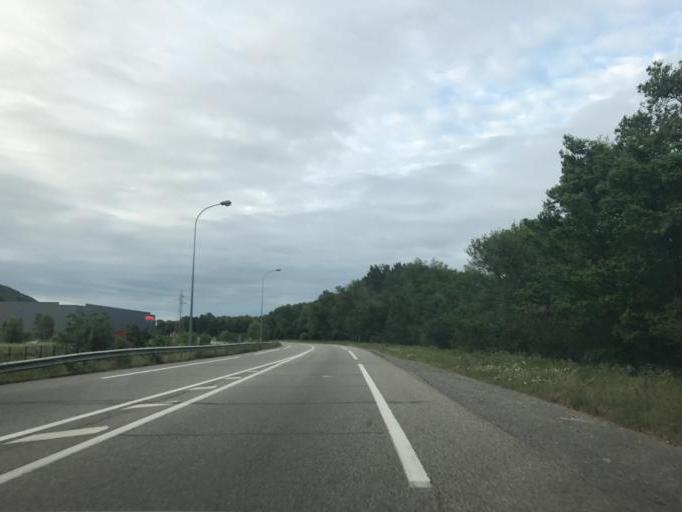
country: FR
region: Rhone-Alpes
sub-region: Departement de l'Ardeche
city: Beauchastel
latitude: 44.8079
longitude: 4.7952
